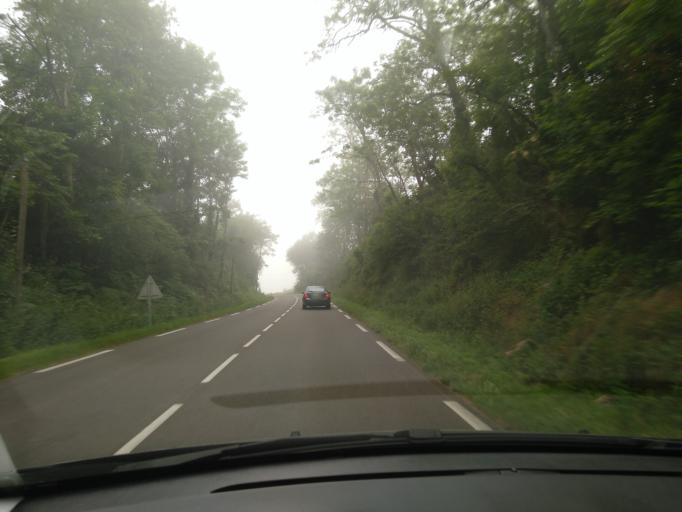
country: FR
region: Aquitaine
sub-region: Departement des Landes
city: Villeneuve-de-Marsan
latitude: 43.8861
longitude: -0.3844
